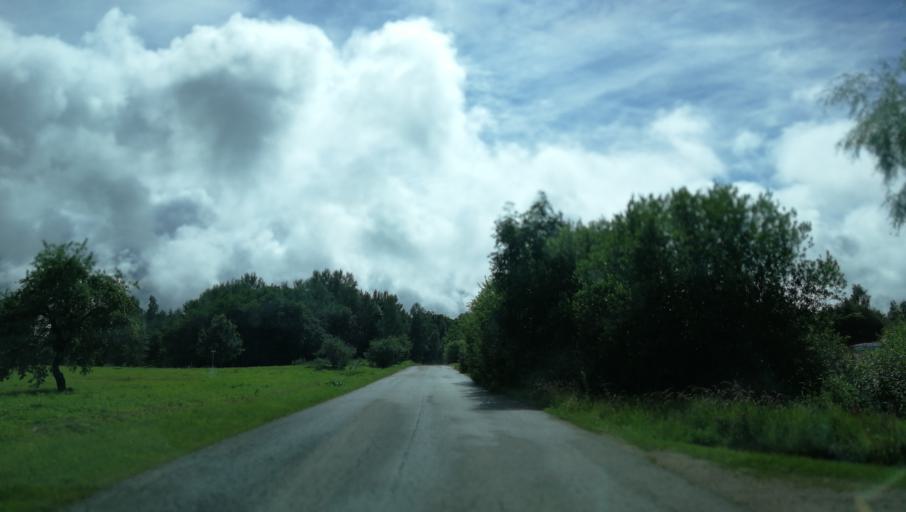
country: LV
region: Cesu Rajons
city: Cesis
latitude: 57.2987
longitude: 25.2618
